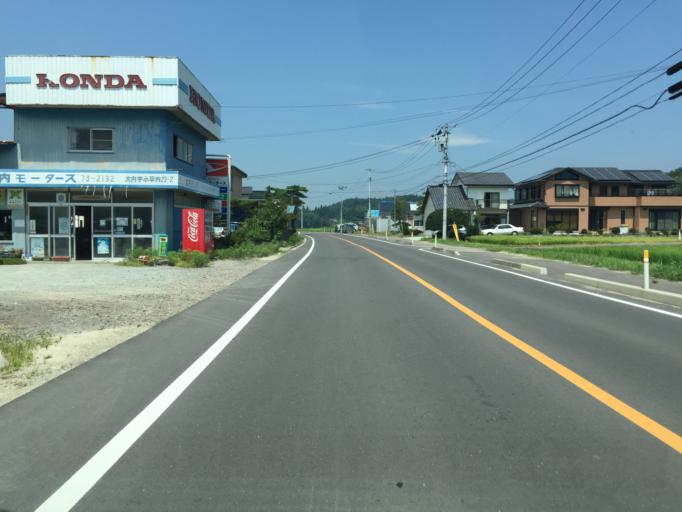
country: JP
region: Miyagi
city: Marumori
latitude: 37.8765
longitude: 140.8230
